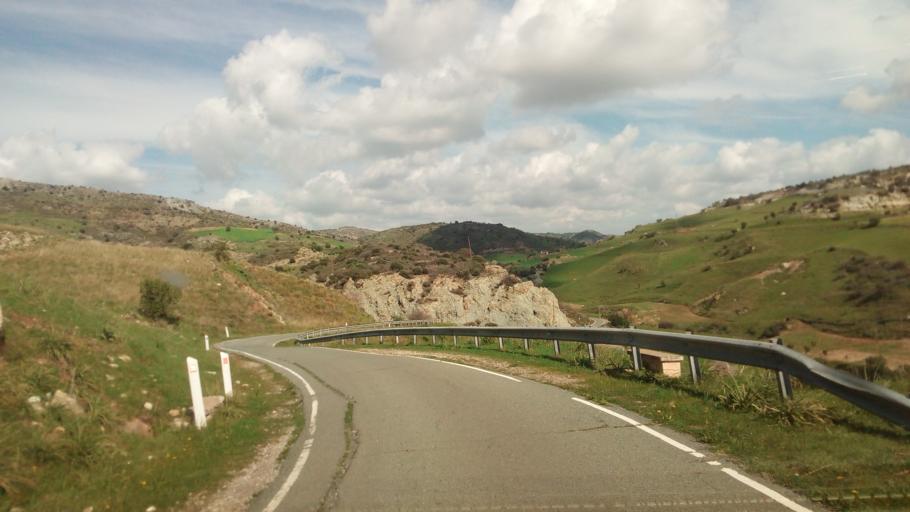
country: CY
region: Pafos
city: Mesogi
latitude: 34.7601
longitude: 32.5520
